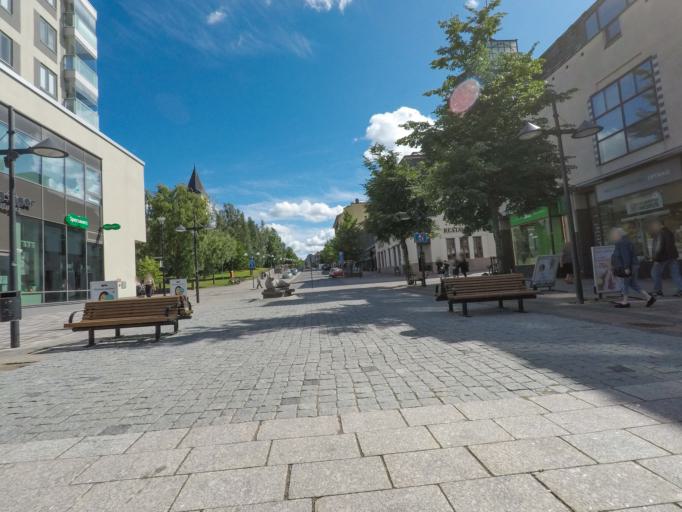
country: FI
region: South Karelia
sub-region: Lappeenranta
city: Lappeenranta
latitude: 61.0587
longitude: 28.1860
